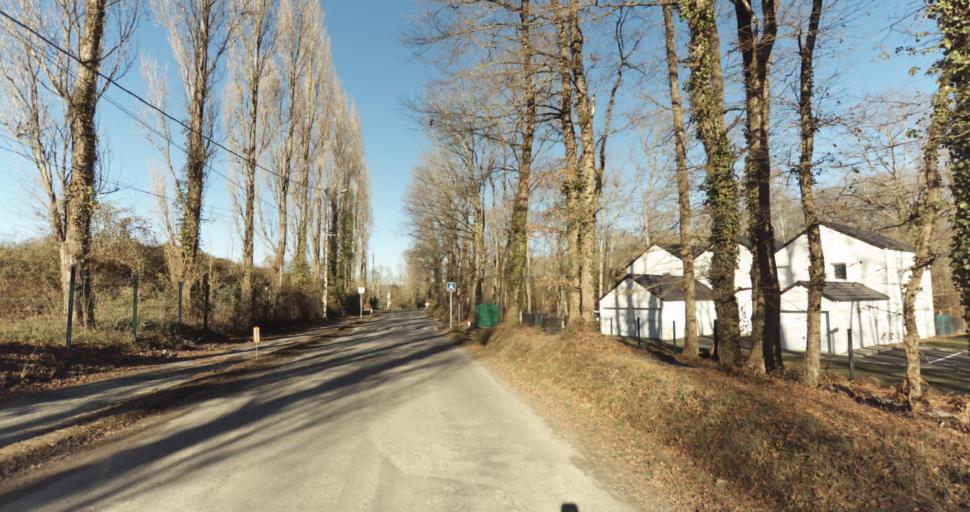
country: FR
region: Aquitaine
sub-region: Departement des Pyrenees-Atlantiques
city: Buros
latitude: 43.3298
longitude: -0.2997
